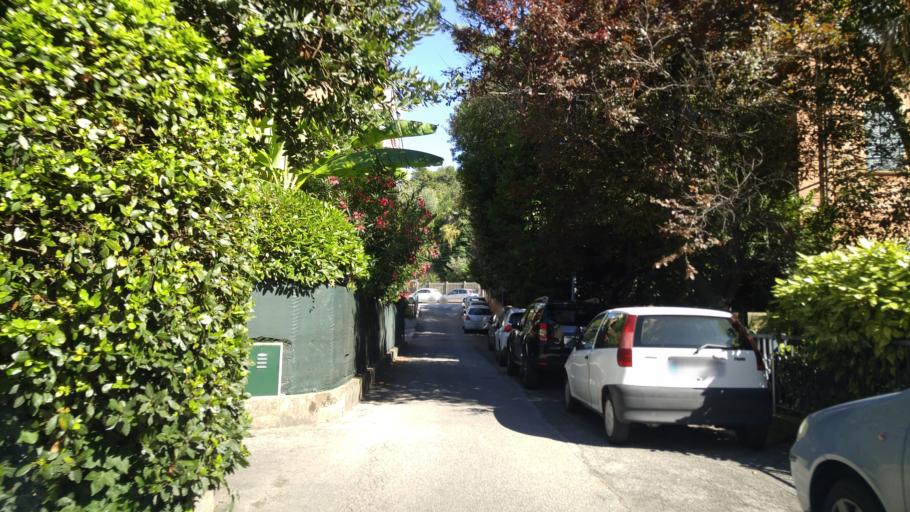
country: IT
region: The Marches
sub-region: Provincia di Pesaro e Urbino
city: Pesaro
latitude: 43.9073
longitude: 12.9218
